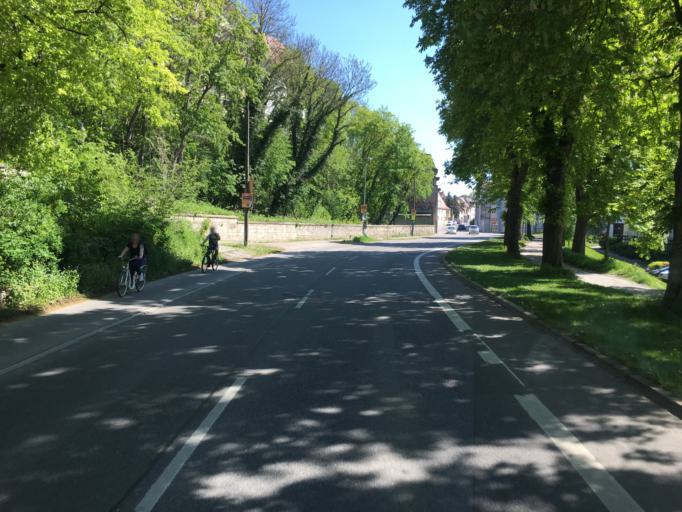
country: DE
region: Saxony-Anhalt
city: Naumburg
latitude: 51.1563
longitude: 11.7996
